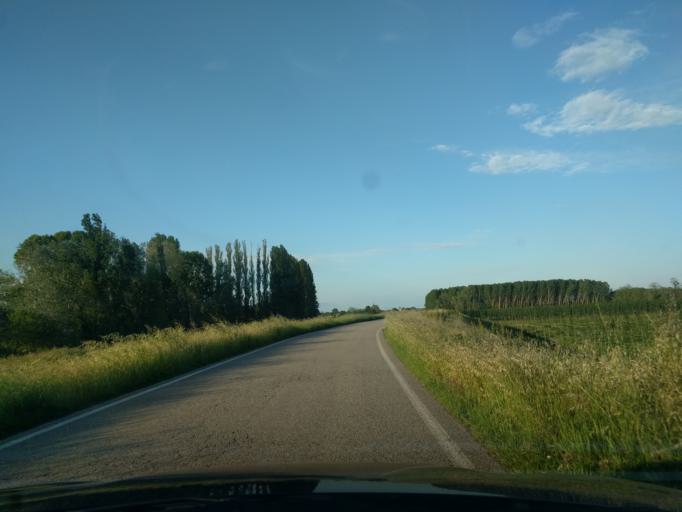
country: IT
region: Veneto
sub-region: Provincia di Rovigo
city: Guarda Veneta
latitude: 44.9741
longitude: 11.7896
